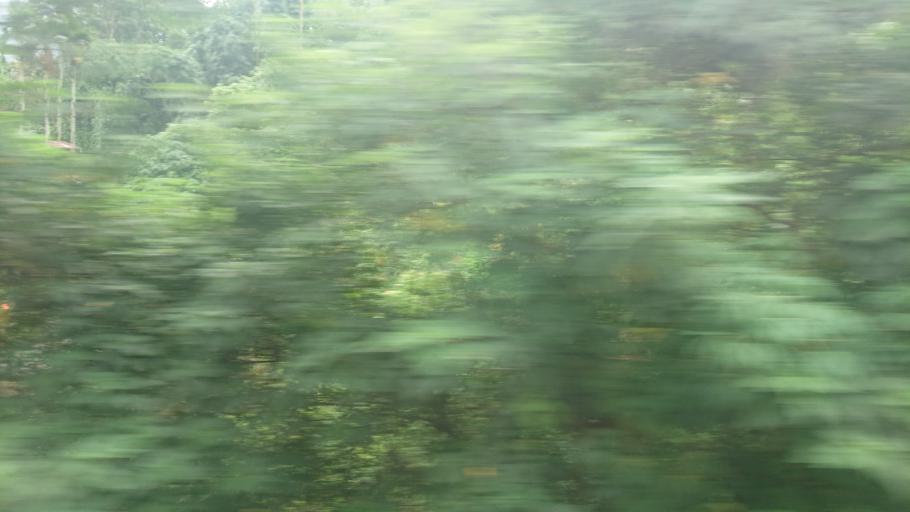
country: TW
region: Taiwan
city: Lugu
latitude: 23.8178
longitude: 120.8491
